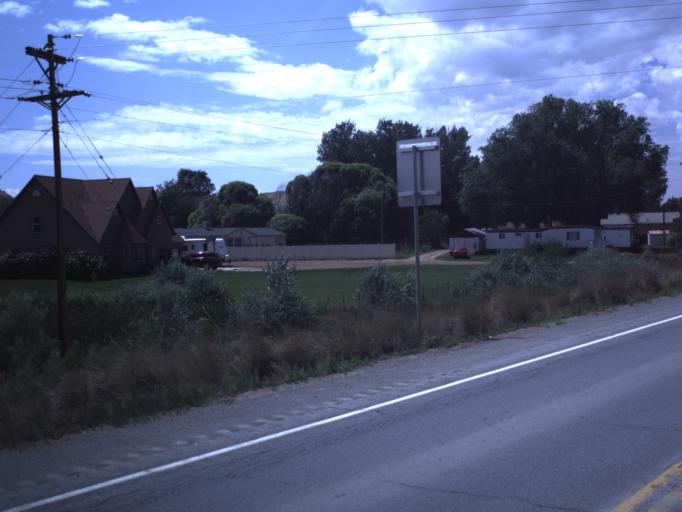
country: US
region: Utah
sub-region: Duchesne County
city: Duchesne
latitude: 40.1618
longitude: -110.3907
